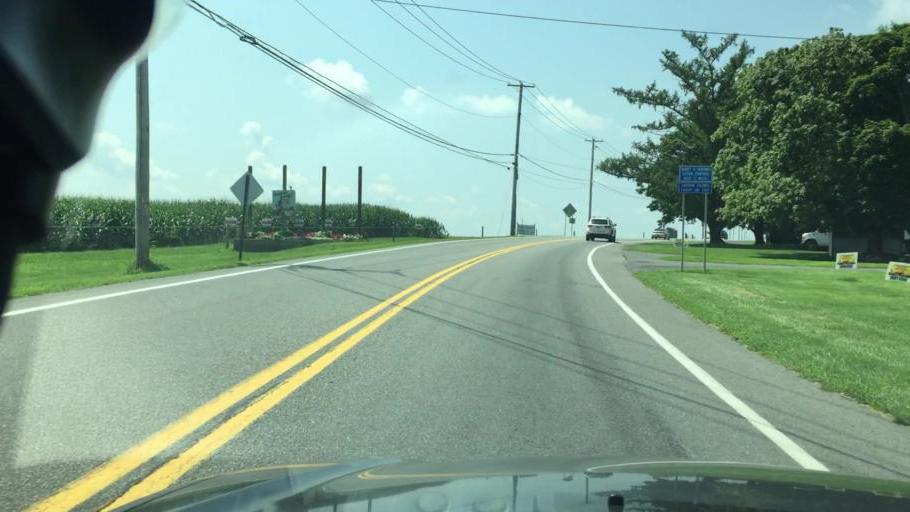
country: US
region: Pennsylvania
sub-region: Columbia County
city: Catawissa
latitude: 40.9273
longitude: -76.4600
